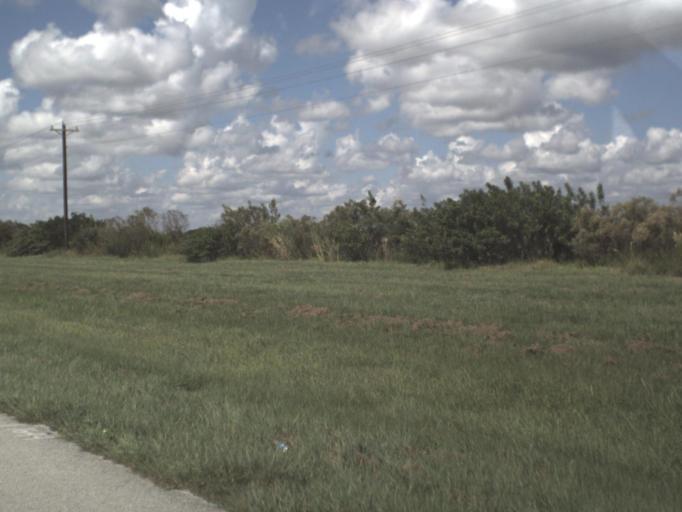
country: US
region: Florida
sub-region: Collier County
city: Immokalee
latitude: 26.4883
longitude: -81.4450
